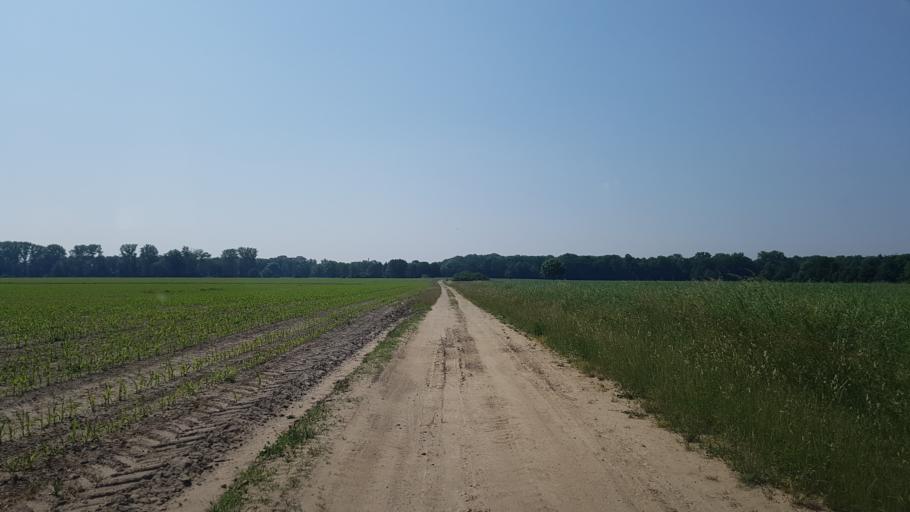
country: DE
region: Brandenburg
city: Sonnewalde
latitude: 51.7108
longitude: 13.6422
